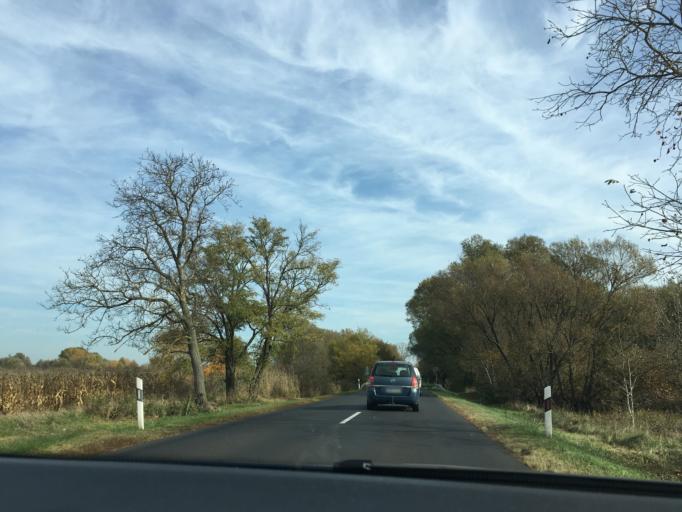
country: HU
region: Szabolcs-Szatmar-Bereg
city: Kisleta
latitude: 47.8555
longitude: 21.9817
